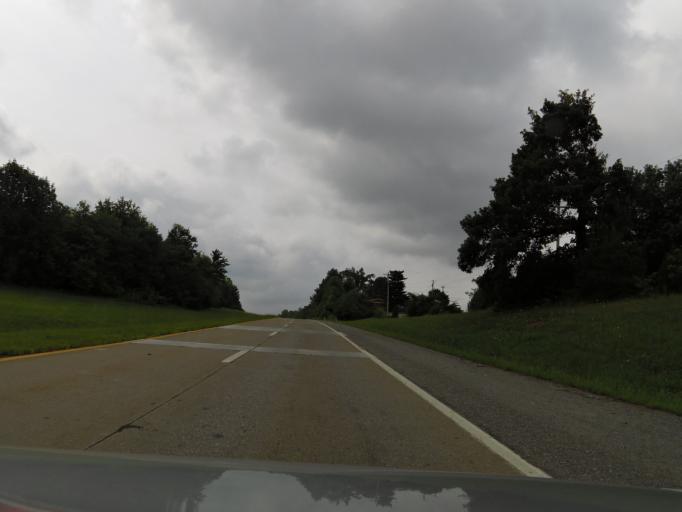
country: US
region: Kentucky
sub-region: Hopkins County
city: Madisonville
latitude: 37.3665
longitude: -87.4923
